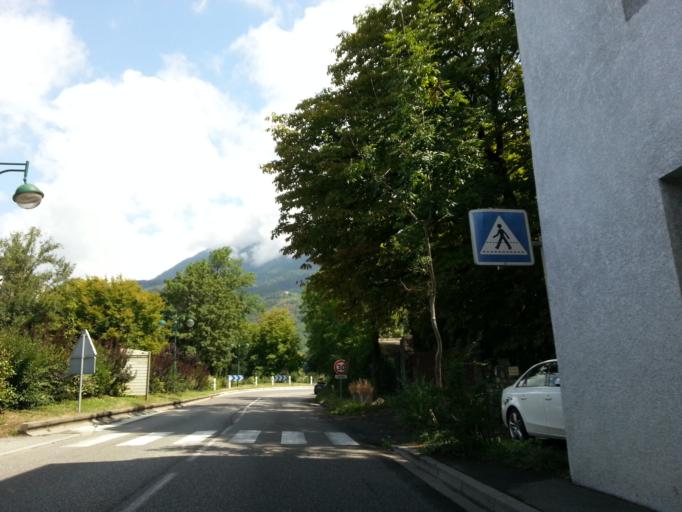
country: FR
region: Rhone-Alpes
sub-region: Departement de la Haute-Savoie
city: Talloires
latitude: 45.8295
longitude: 6.2053
